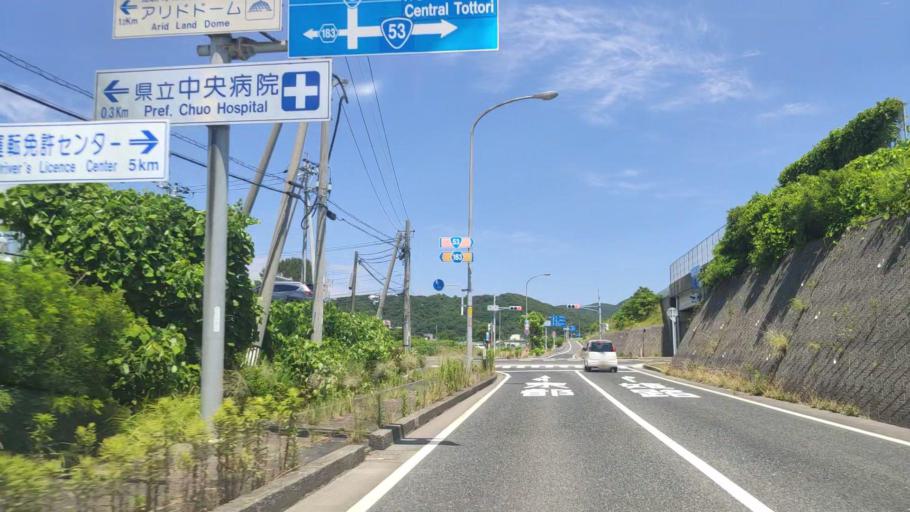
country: JP
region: Tottori
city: Tottori
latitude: 35.5220
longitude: 134.2156
